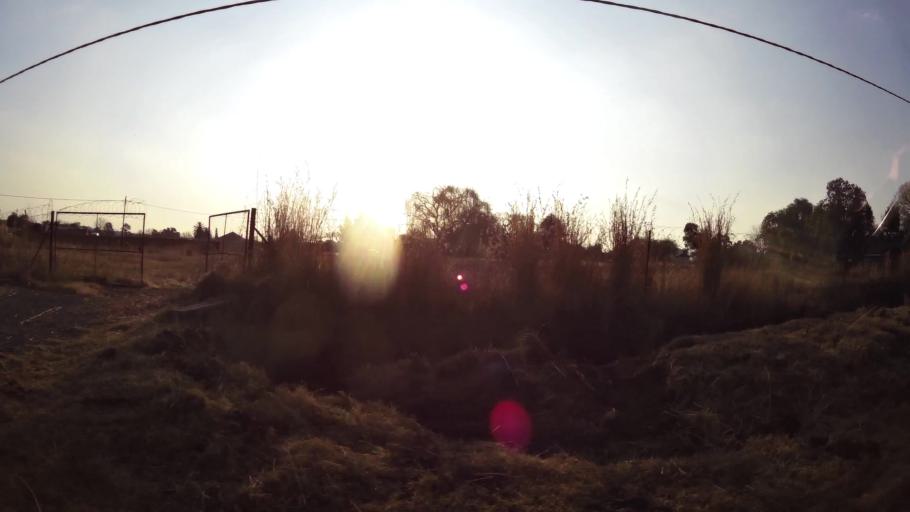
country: ZA
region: Gauteng
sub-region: Ekurhuleni Metropolitan Municipality
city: Benoni
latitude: -26.1573
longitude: 28.3685
